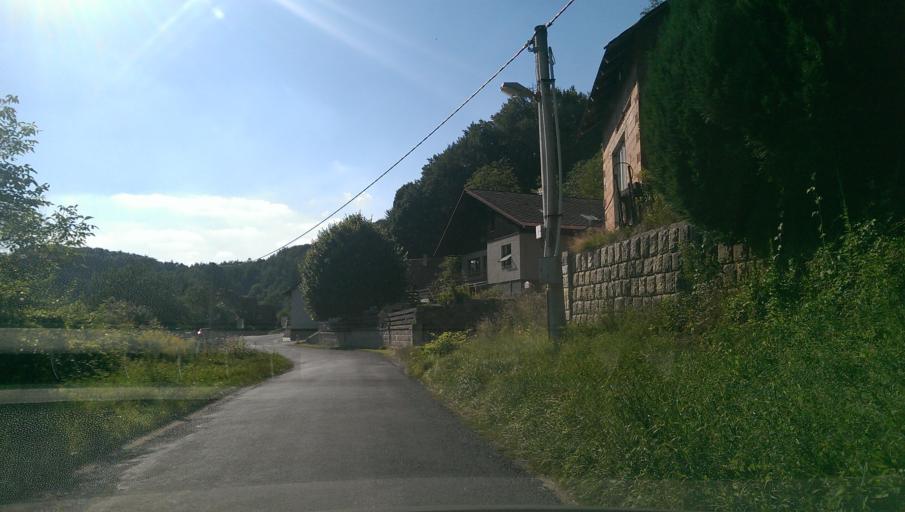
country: CZ
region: Liberecky
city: Mala Skala
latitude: 50.6205
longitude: 15.1894
